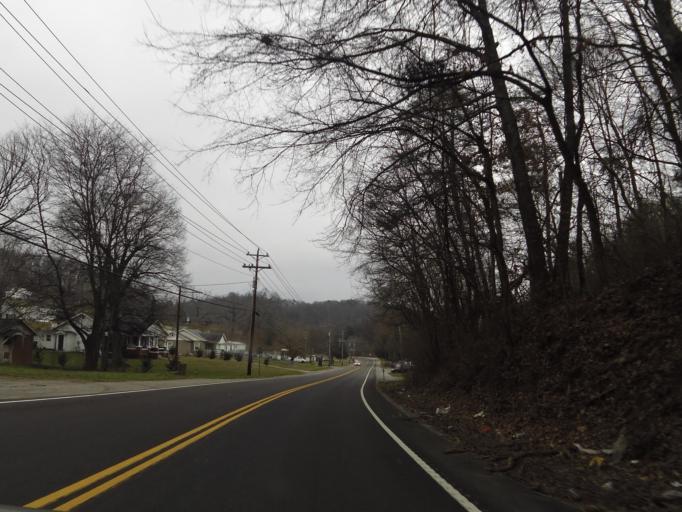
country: US
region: Tennessee
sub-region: Anderson County
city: Clinton
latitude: 36.1264
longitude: -84.1452
